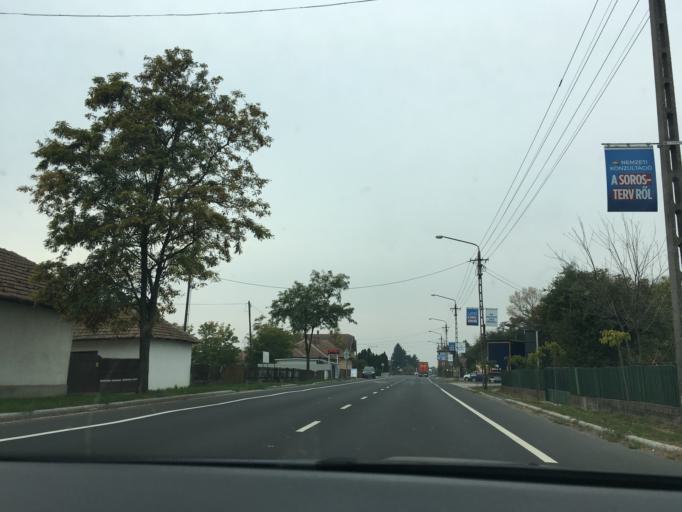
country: HU
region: Jasz-Nagykun-Szolnok
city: Kenderes
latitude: 47.2470
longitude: 20.6676
